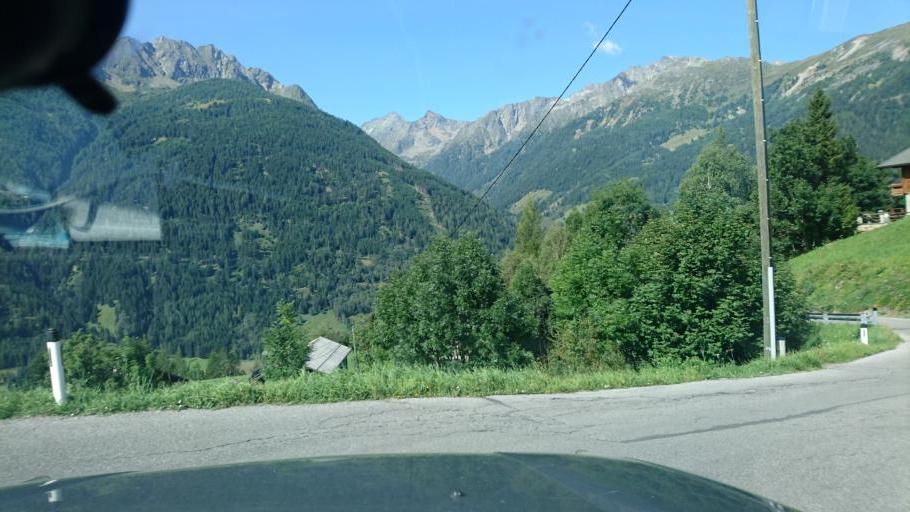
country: AT
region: Carinthia
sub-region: Politischer Bezirk Spittal an der Drau
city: Grosskirchheim
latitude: 46.9864
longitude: 12.8889
